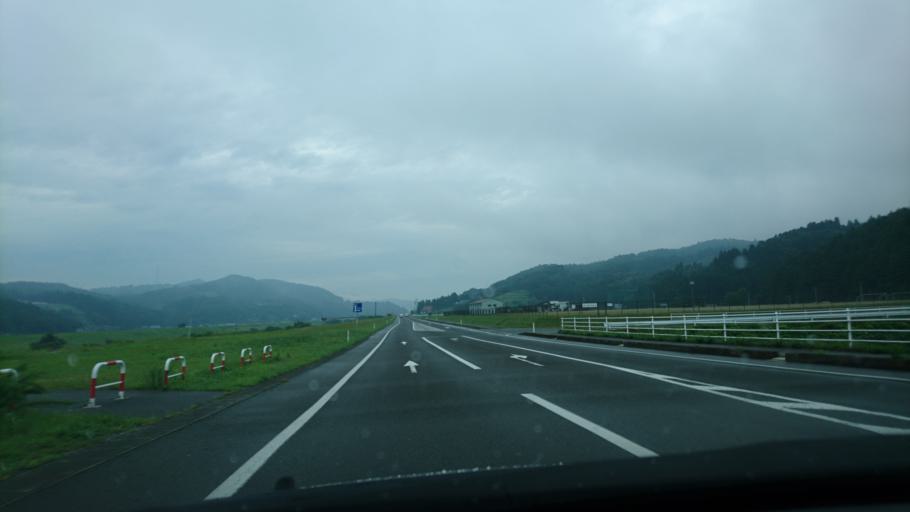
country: JP
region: Iwate
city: Ichinoseki
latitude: 38.9058
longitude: 141.2600
